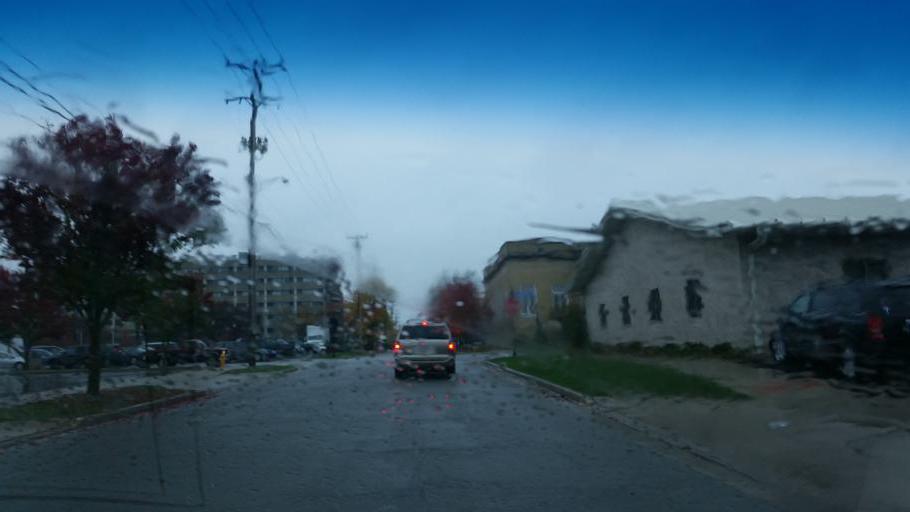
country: US
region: Indiana
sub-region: Howard County
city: Kokomo
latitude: 40.4879
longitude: -86.1288
